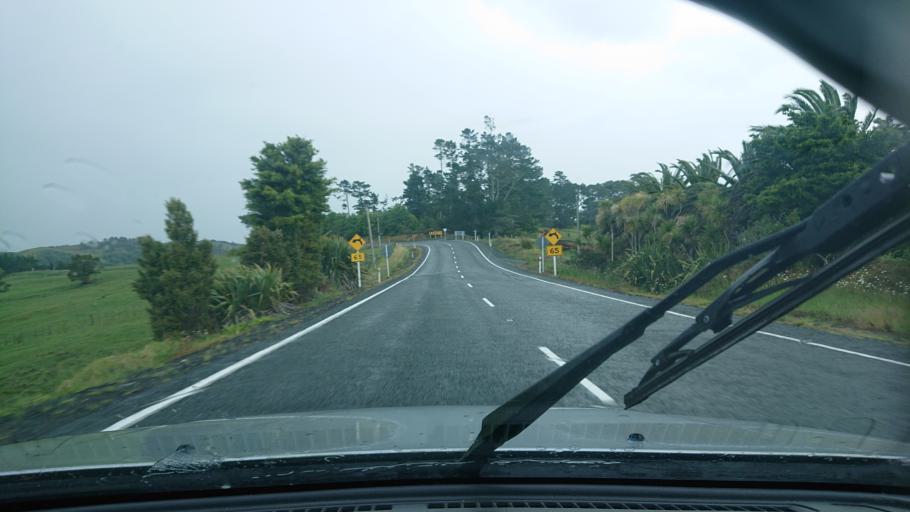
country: NZ
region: Auckland
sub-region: Auckland
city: Wellsford
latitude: -36.3356
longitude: 174.4690
